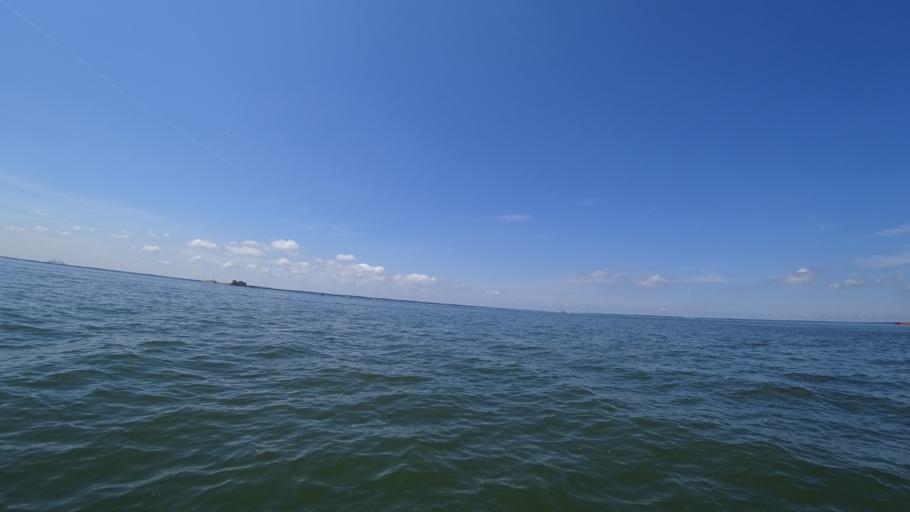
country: US
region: Virginia
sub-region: City of Newport News
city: Newport News
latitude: 36.9589
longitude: -76.4066
